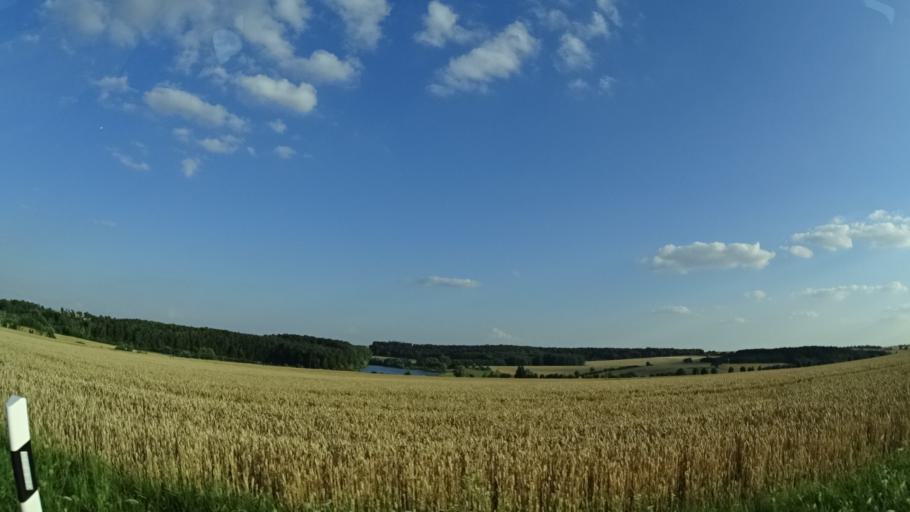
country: DE
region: Thuringia
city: Henneberg
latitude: 50.4551
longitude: 10.3790
